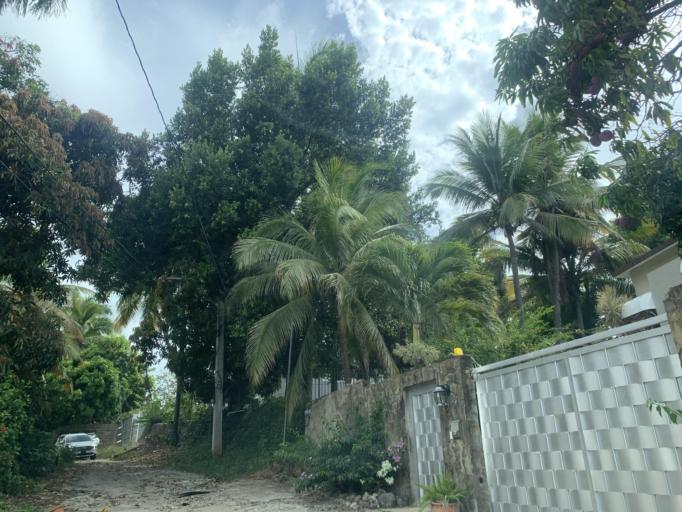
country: DO
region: Puerto Plata
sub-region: Puerto Plata
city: Puerto Plata
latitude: 19.8137
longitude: -70.7214
